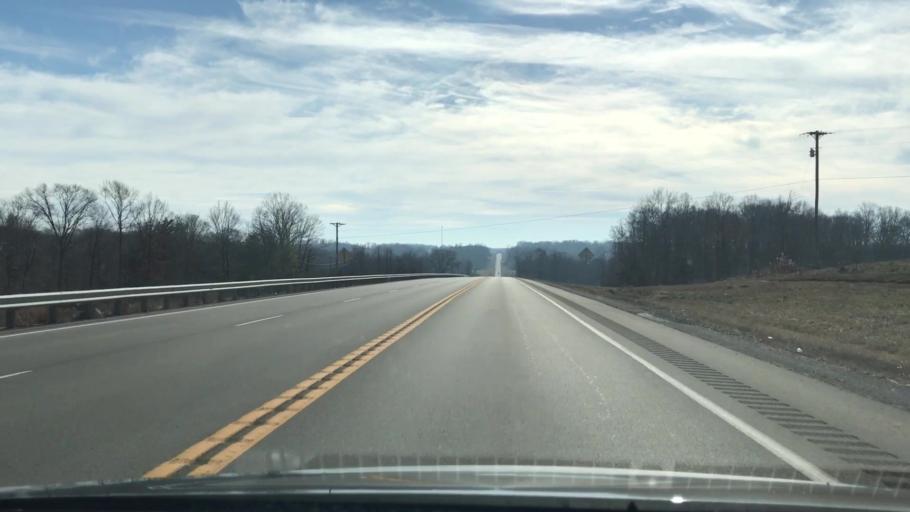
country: US
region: Kentucky
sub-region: Monroe County
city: Tompkinsville
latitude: 36.8146
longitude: -85.6882
